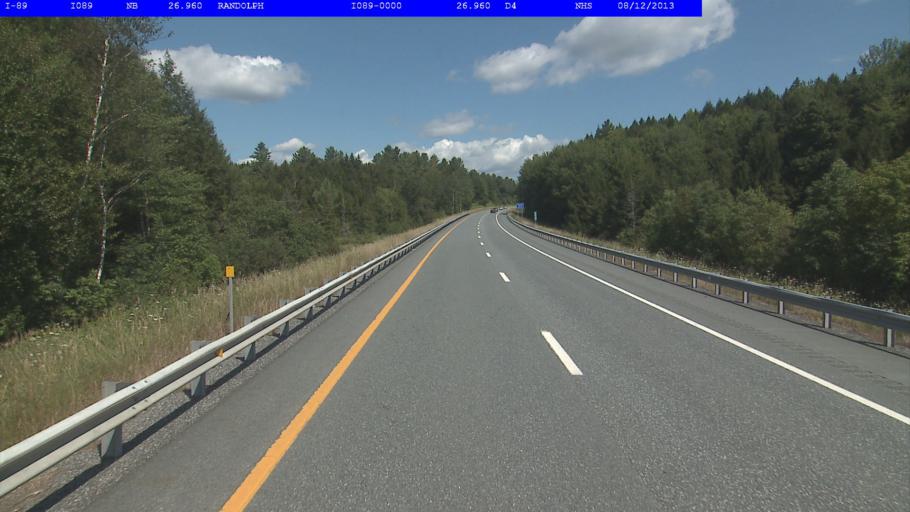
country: US
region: Vermont
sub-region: Orange County
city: Randolph
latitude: 43.8887
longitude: -72.6164
